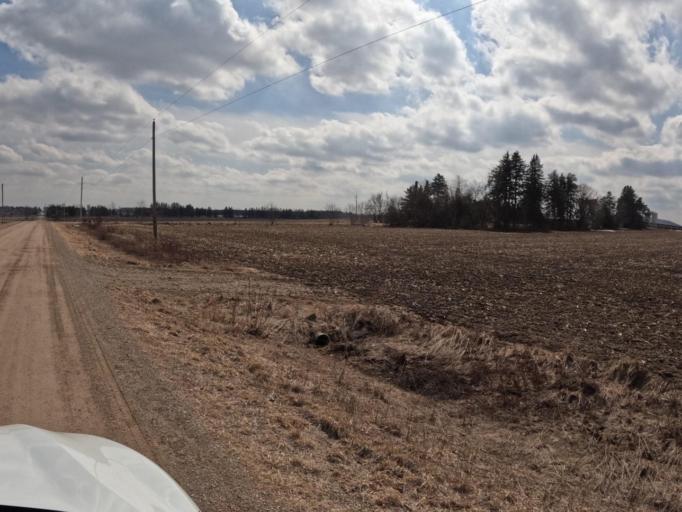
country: CA
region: Ontario
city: Shelburne
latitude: 43.9745
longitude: -80.2680
